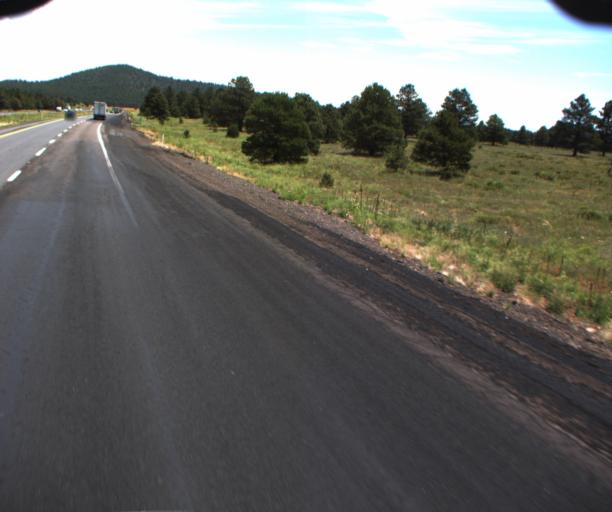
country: US
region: Arizona
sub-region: Coconino County
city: Williams
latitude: 35.2583
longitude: -112.0974
